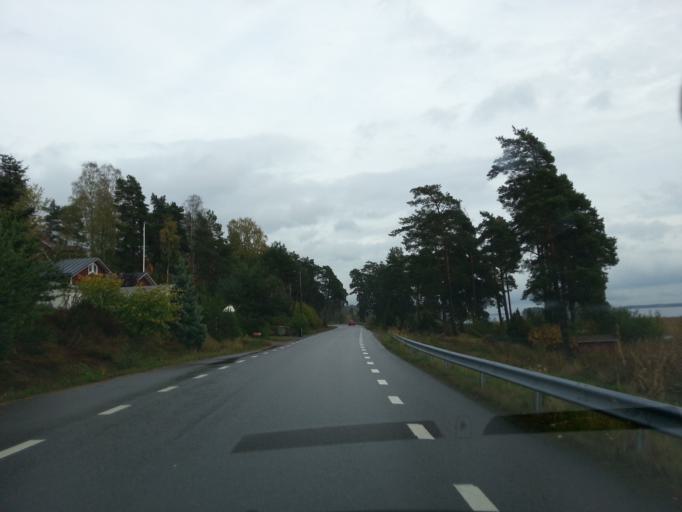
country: SE
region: OEstergoetland
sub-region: Norrkopings Kommun
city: Krokek
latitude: 58.6671
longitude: 16.3354
